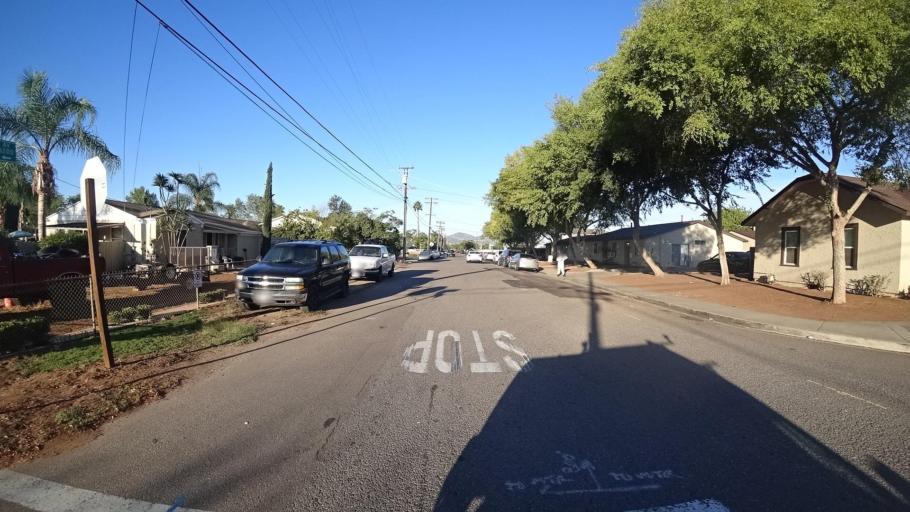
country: US
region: California
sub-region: San Diego County
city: Bostonia
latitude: 32.8115
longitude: -116.9403
